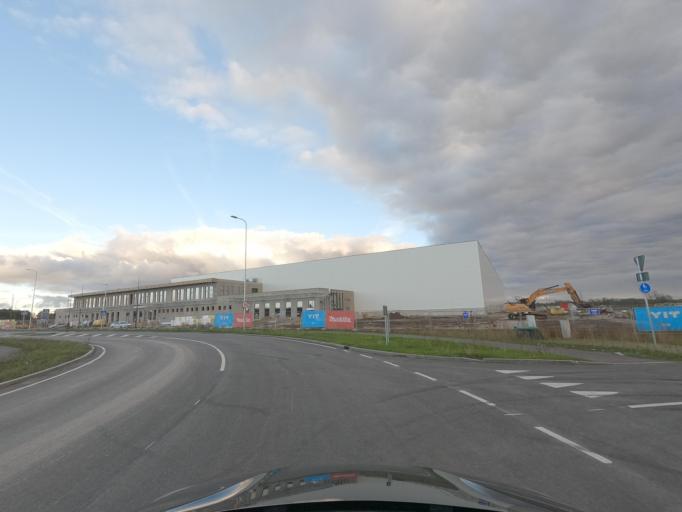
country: EE
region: Harju
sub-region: Saue vald
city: Laagri
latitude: 59.3343
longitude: 24.5987
